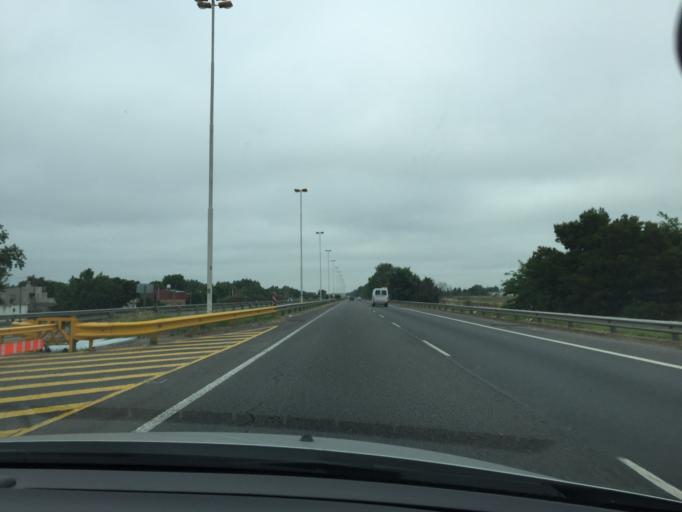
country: AR
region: Buenos Aires
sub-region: Partido de Ezeiza
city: Ezeiza
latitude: -34.8423
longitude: -58.5292
